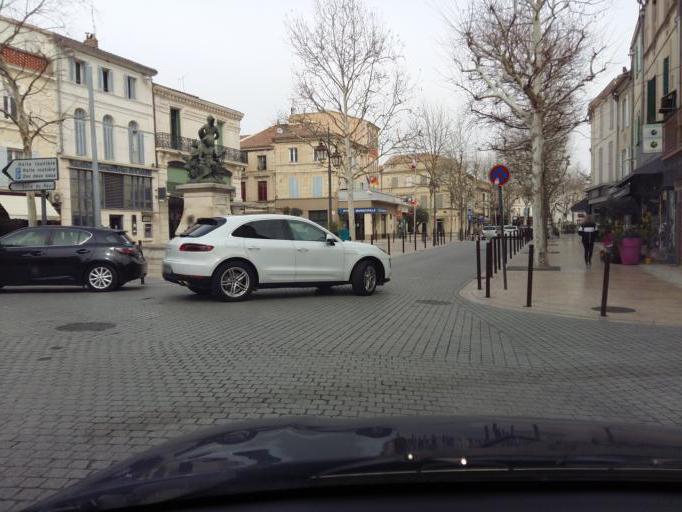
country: FR
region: Provence-Alpes-Cote d'Azur
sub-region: Departement des Bouches-du-Rhone
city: Chateaurenard
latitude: 43.8822
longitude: 4.8541
